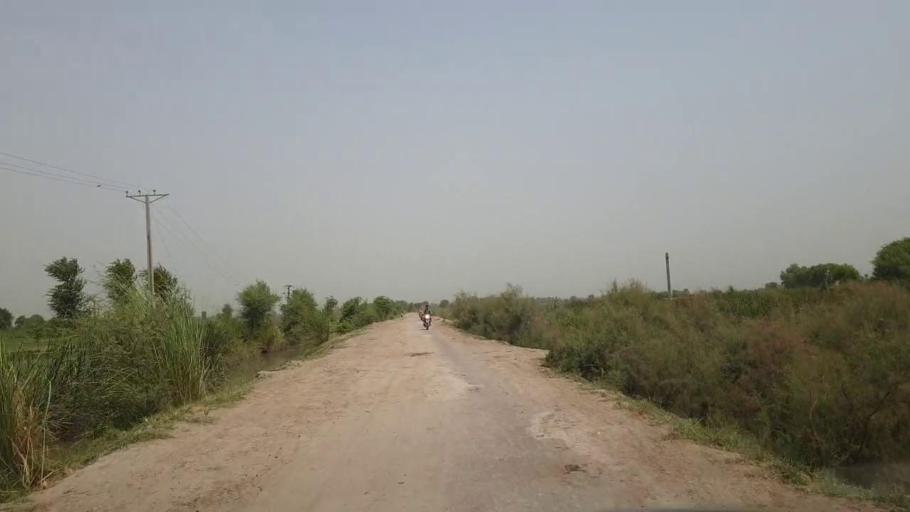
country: PK
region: Sindh
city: Gambat
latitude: 27.4477
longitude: 68.4441
